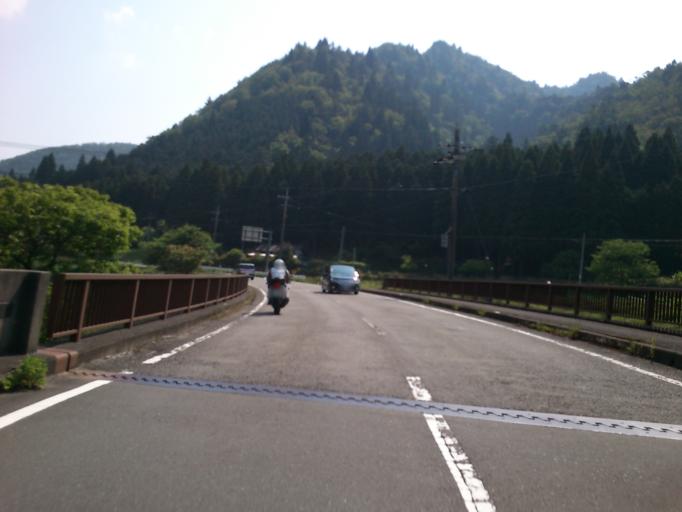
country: JP
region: Kyoto
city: Kameoka
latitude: 35.2529
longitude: 135.5627
